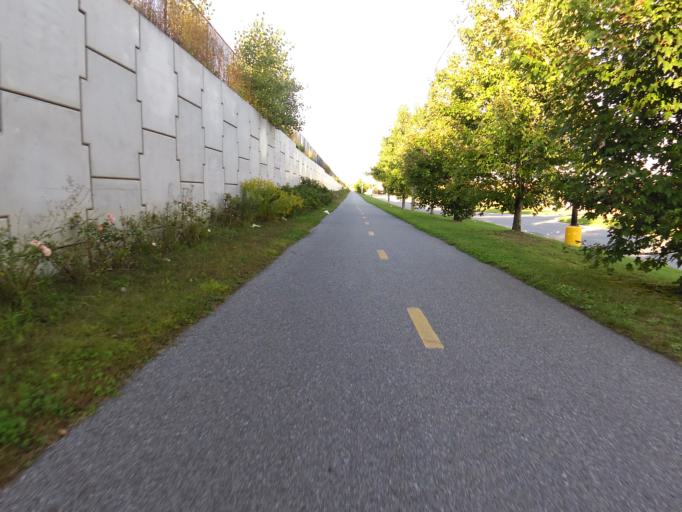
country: CA
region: Quebec
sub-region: Outaouais
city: Gatineau
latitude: 45.4657
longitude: -75.7211
